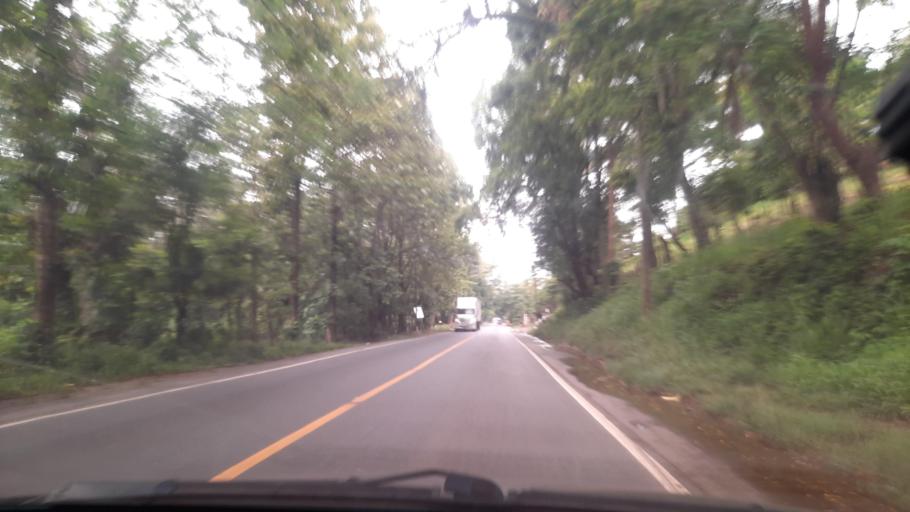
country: GT
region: Izabal
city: Morales
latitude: 15.4297
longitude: -88.9732
